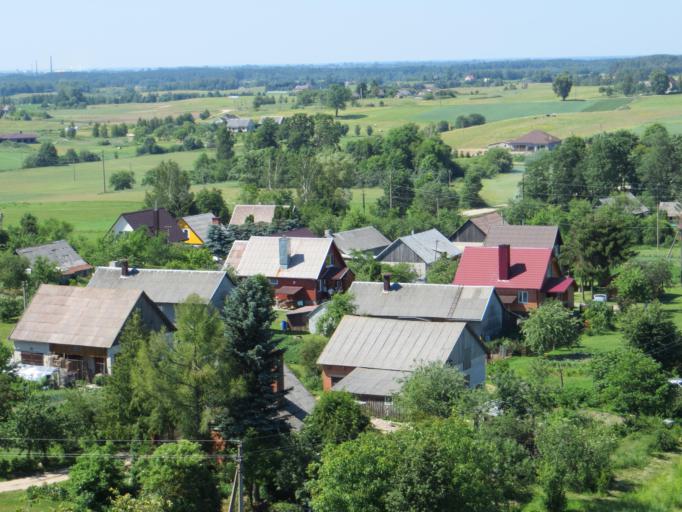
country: LT
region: Alytaus apskritis
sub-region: Alytus
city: Alytus
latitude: 54.3857
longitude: 24.1357
